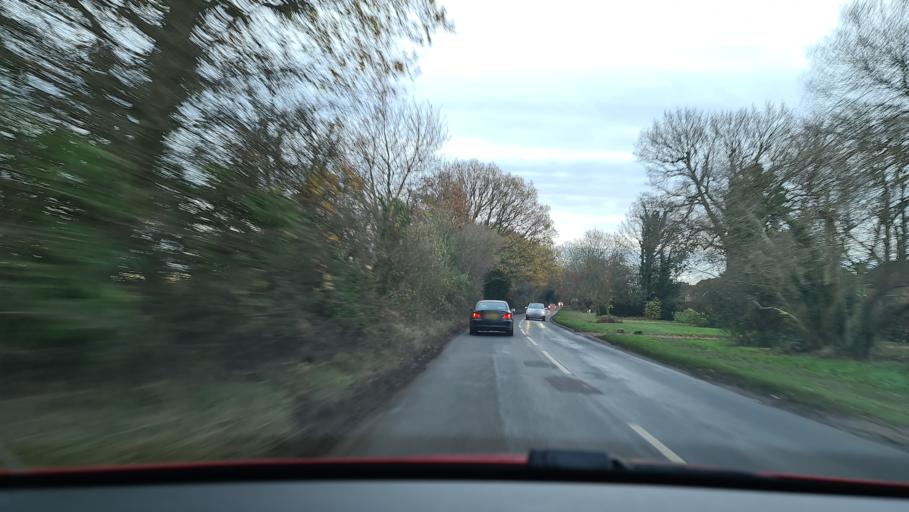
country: GB
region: England
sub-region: Buckinghamshire
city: Amersham
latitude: 51.6915
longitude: -0.6481
